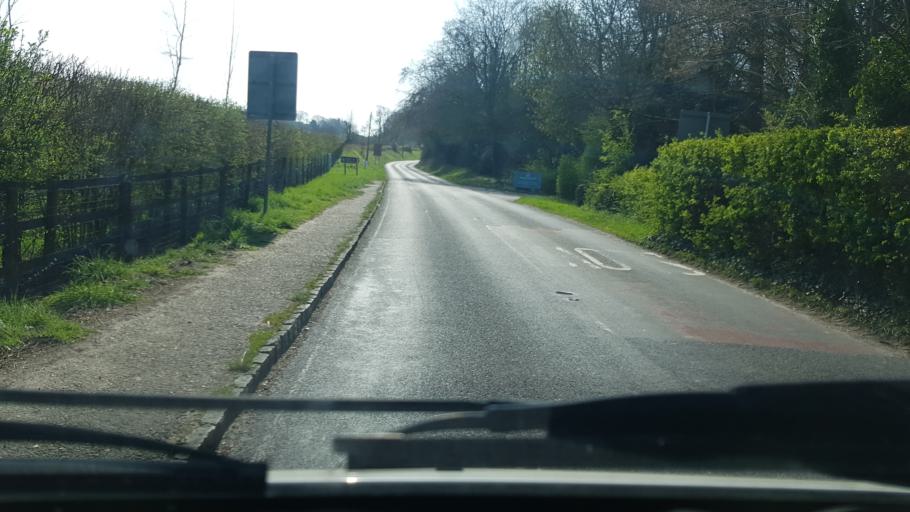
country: GB
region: England
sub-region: West Sussex
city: Boxgrove
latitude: 50.9090
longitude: -0.7562
